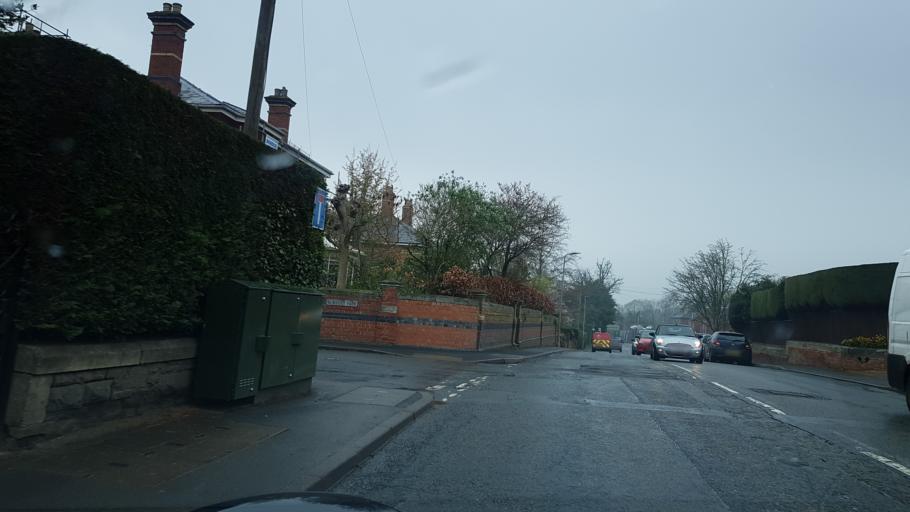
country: GB
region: England
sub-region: Herefordshire
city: Ledbury
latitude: 52.0430
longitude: -2.4260
